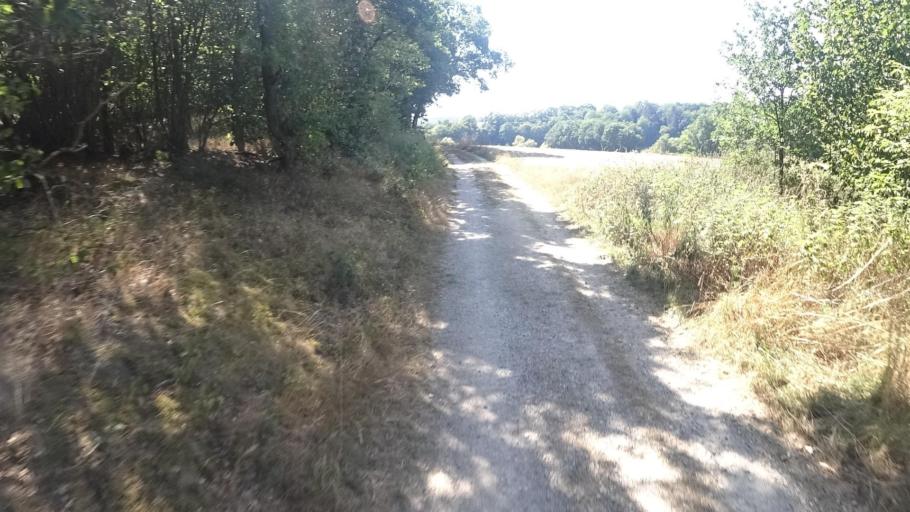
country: DE
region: Rheinland-Pfalz
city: Belgweiler
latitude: 49.9541
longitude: 7.4920
